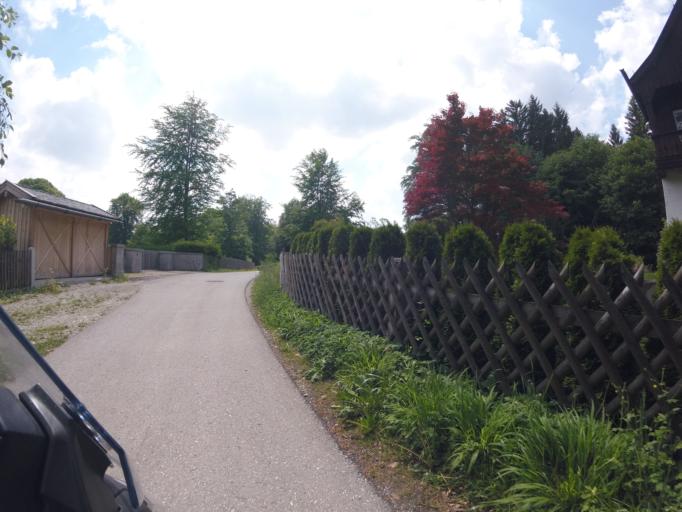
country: DE
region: Bavaria
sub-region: Upper Bavaria
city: Icking
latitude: 47.9367
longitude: 11.4283
